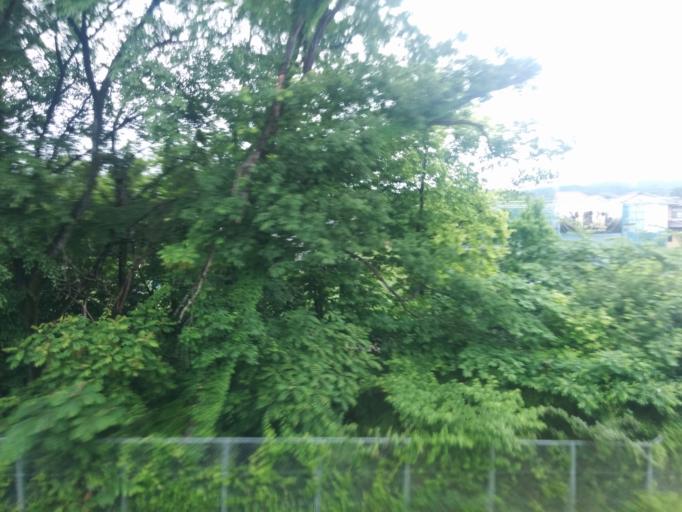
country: JP
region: Tochigi
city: Imaichi
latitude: 36.6835
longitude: 139.7334
